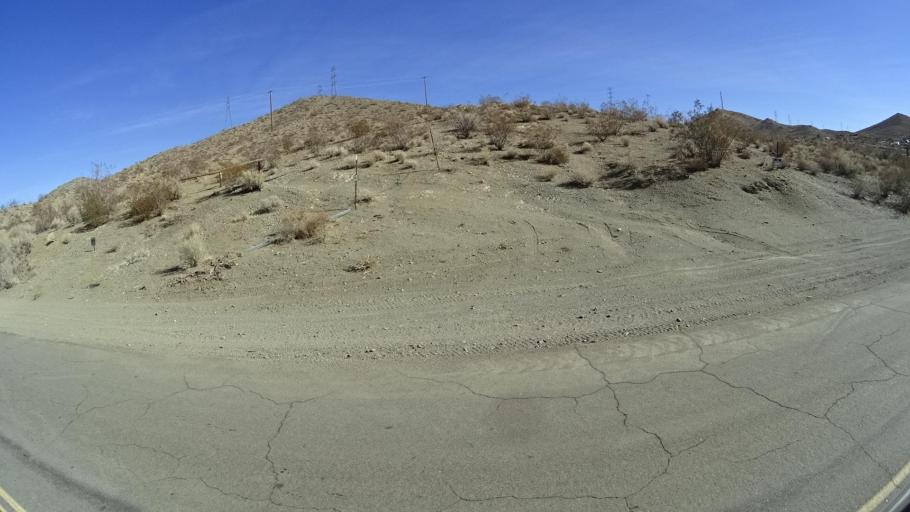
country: US
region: California
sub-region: Kern County
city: Ridgecrest
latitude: 35.3724
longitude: -117.6565
